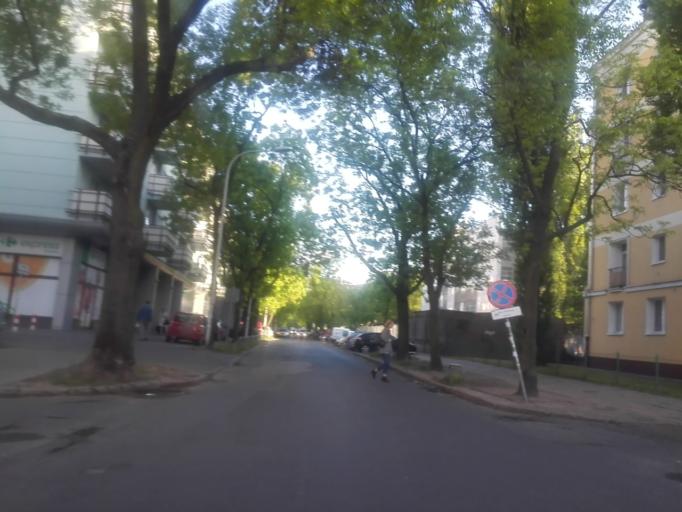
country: PL
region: Masovian Voivodeship
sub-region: Warszawa
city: Mokotow
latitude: 52.2061
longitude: 21.0455
